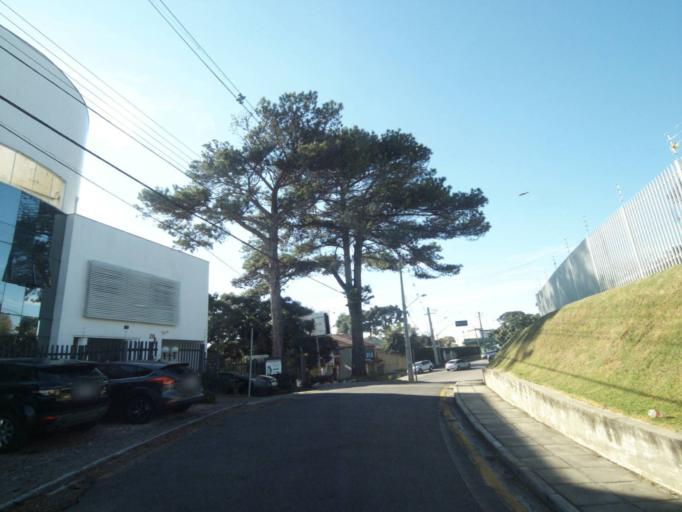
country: BR
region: Parana
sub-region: Curitiba
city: Curitiba
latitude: -25.4249
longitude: -49.3015
